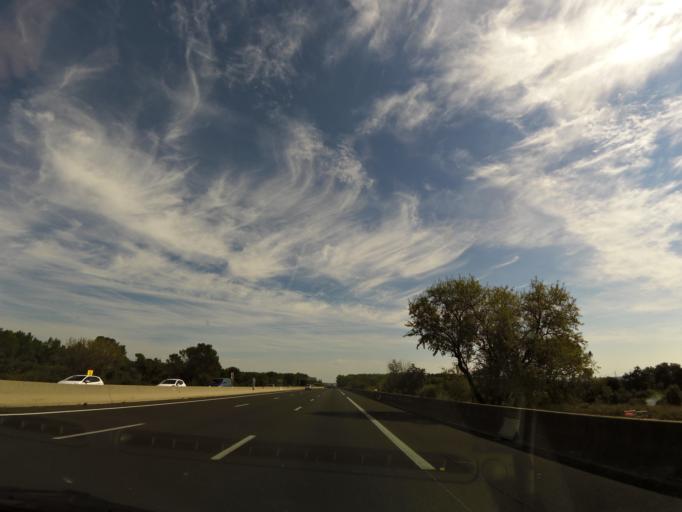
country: FR
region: Languedoc-Roussillon
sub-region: Departement du Gard
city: Vergeze
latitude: 43.7501
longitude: 4.2291
